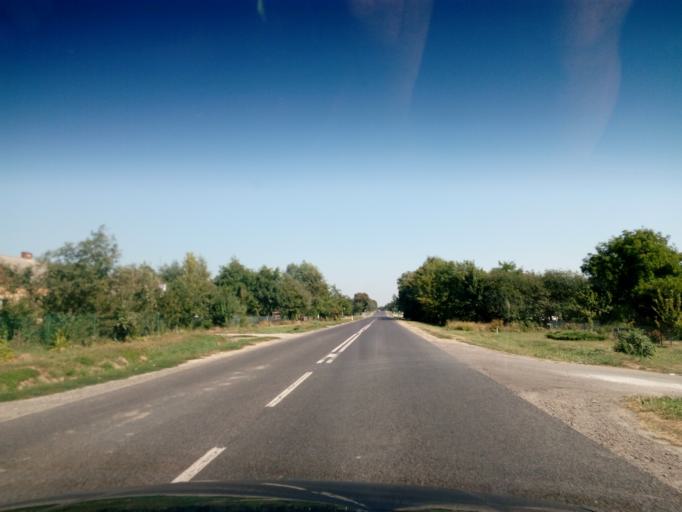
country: PL
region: Lublin Voivodeship
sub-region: Powiat hrubieszowski
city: Horodlo
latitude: 50.8438
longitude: 24.0506
